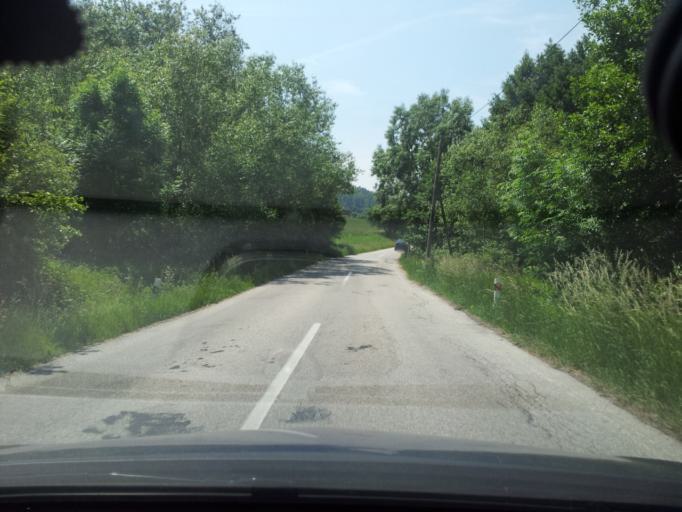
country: SK
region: Nitriansky
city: Zlate Moravce
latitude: 48.5045
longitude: 18.4322
